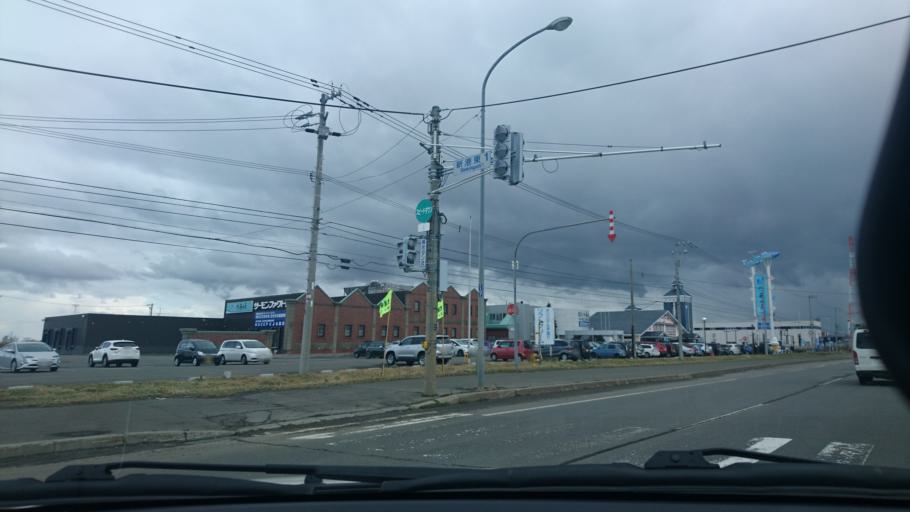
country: JP
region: Hokkaido
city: Ishikari
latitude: 43.2082
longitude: 141.3331
